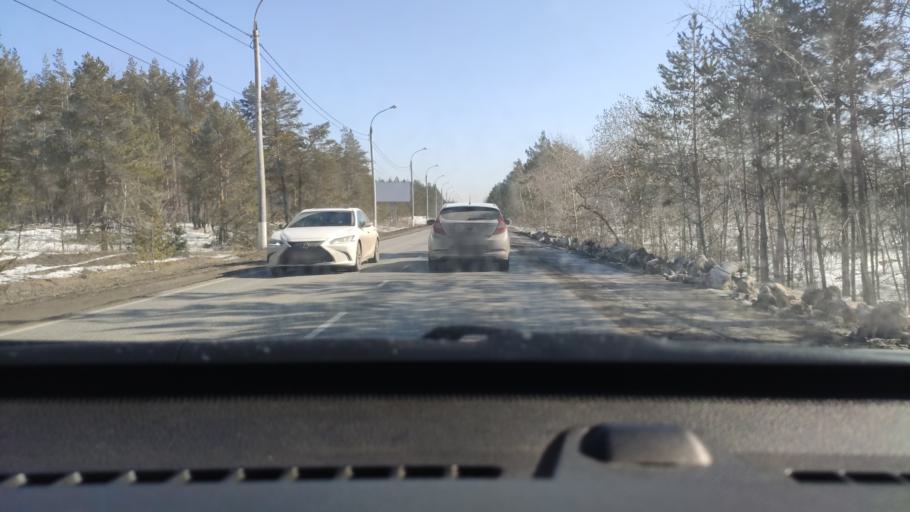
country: RU
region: Samara
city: Zhigulevsk
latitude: 53.4018
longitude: 49.5029
